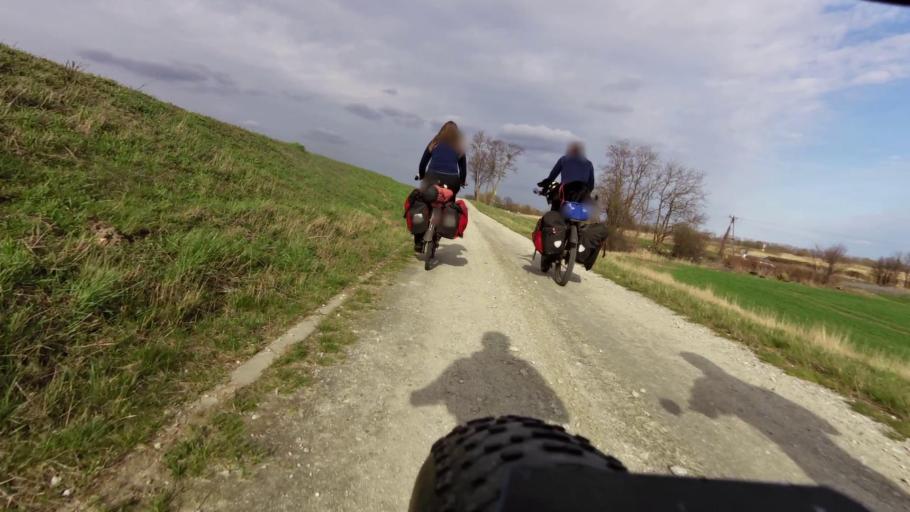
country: PL
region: Lubusz
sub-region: Powiat gorzowski
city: Kostrzyn nad Odra
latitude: 52.5602
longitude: 14.6319
